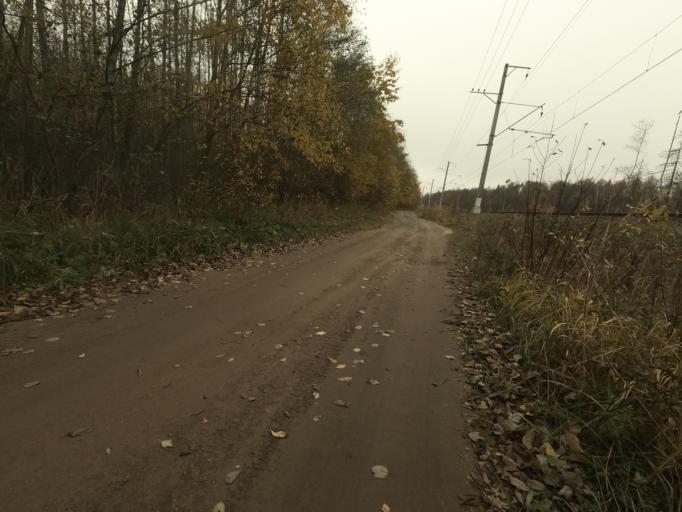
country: RU
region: Leningrad
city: Pavlovo
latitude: 59.7855
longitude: 30.8920
